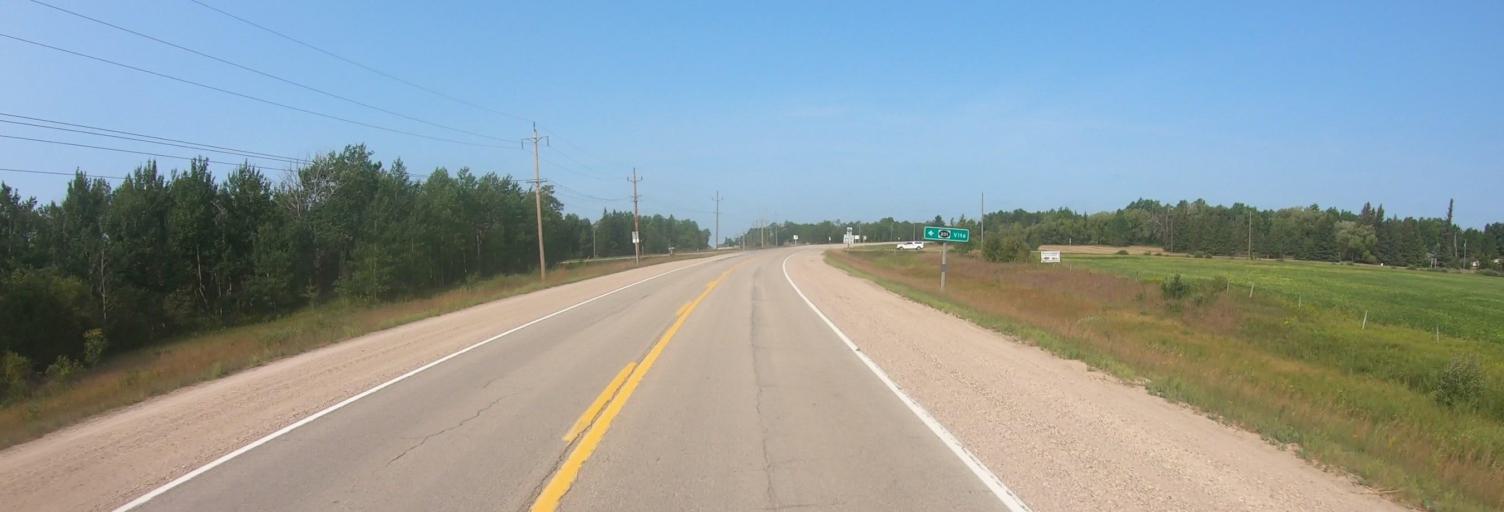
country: US
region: Minnesota
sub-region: Roseau County
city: Roseau
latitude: 49.0896
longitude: -95.9766
